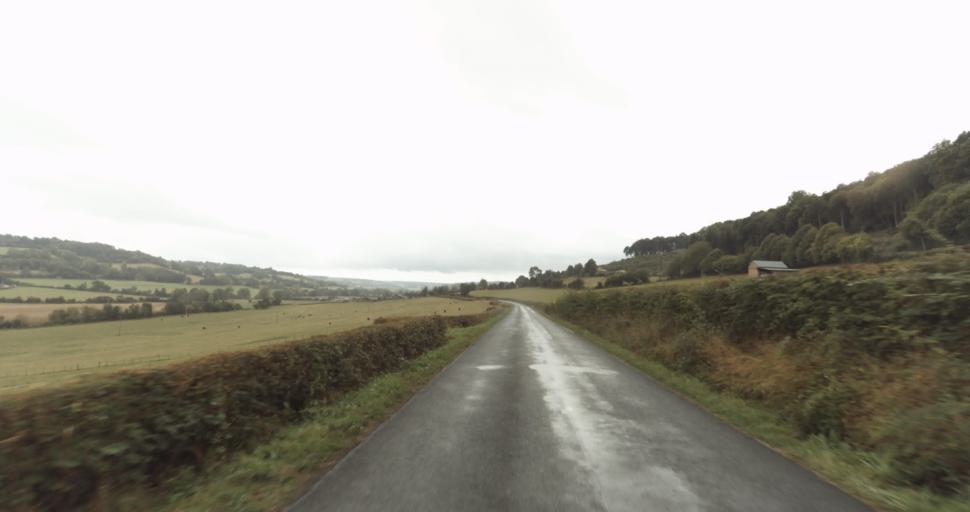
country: FR
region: Lower Normandy
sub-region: Departement de l'Orne
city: Vimoutiers
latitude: 48.9032
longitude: 0.2081
